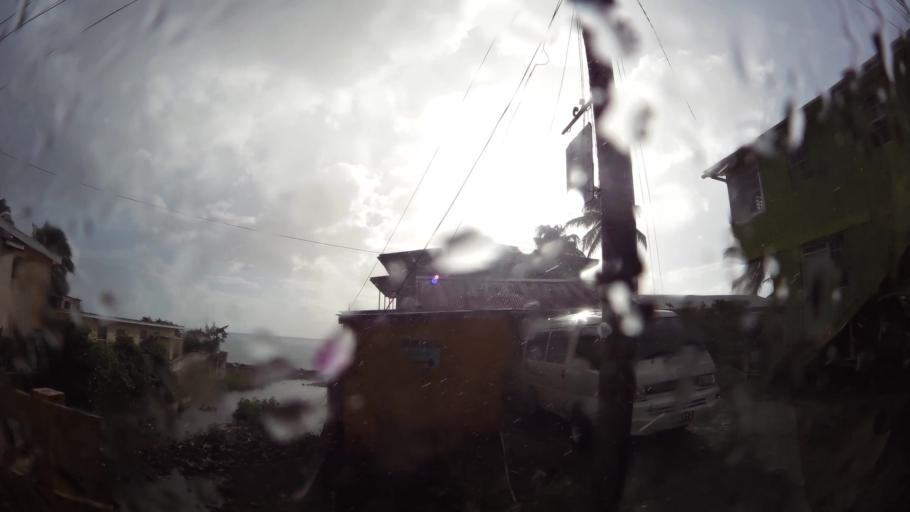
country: DM
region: Saint Paul
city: Mahaut
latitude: 15.3621
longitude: -61.3977
